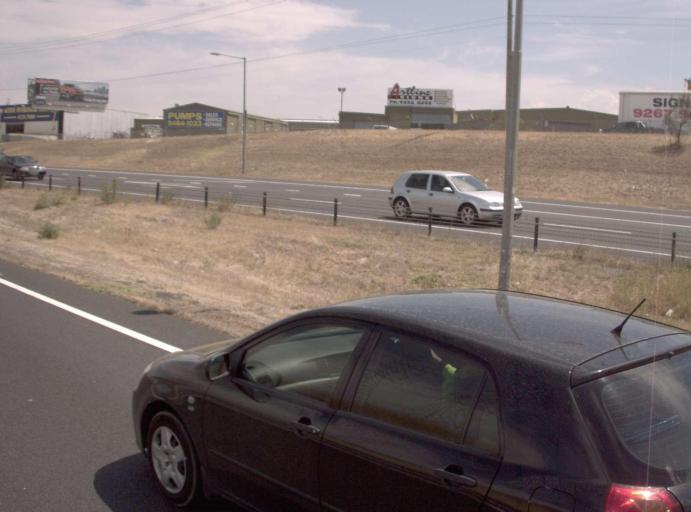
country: AU
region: Victoria
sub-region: Moonee Valley
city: Keilor East
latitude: -37.7315
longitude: 144.8551
